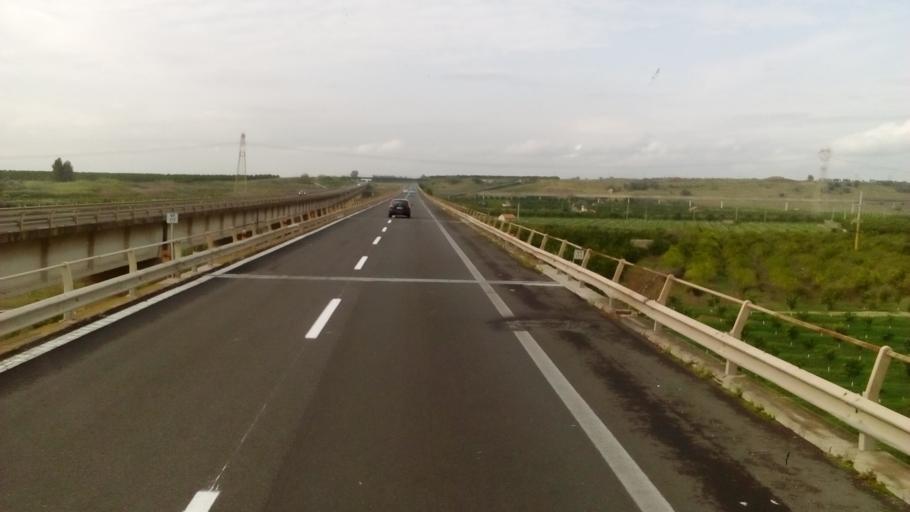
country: IT
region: Sicily
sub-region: Catania
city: Motta Sant'Anastasia
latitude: 37.4685
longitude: 14.8840
